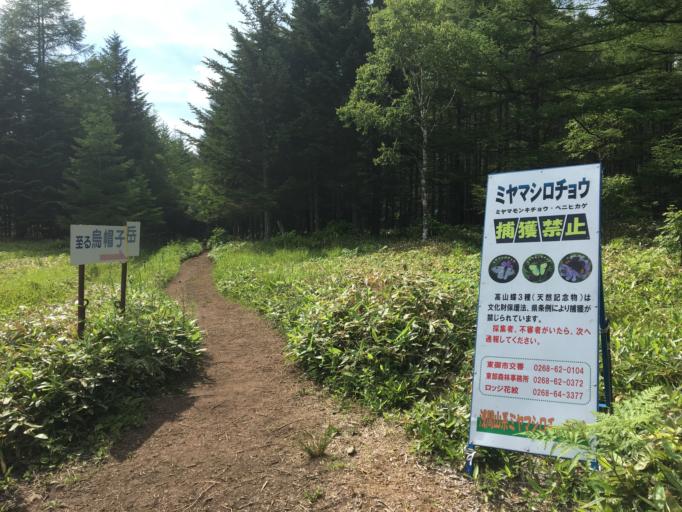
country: JP
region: Nagano
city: Komoro
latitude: 36.4283
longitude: 138.4121
